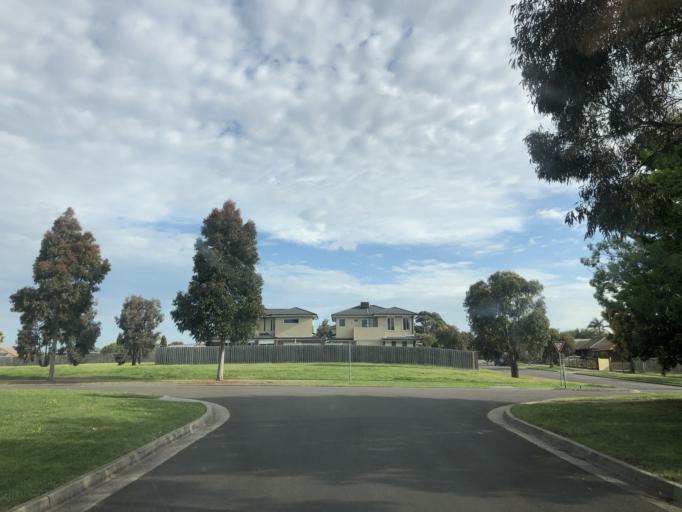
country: AU
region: Victoria
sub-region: Casey
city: Hampton Park
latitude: -38.0220
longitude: 145.2550
